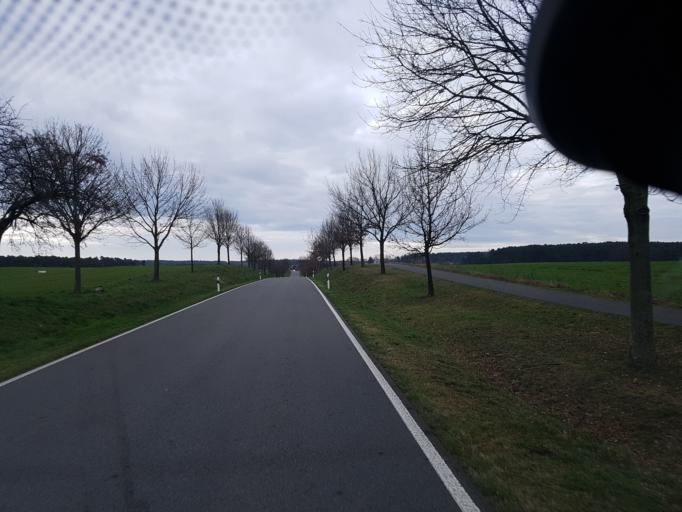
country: DE
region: Brandenburg
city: Gross Lindow
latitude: 52.1529
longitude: 14.5209
